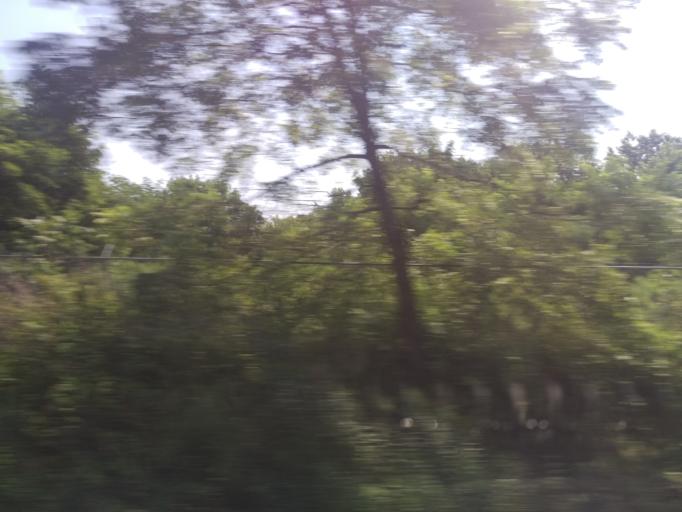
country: CA
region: Ontario
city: Ajax
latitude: 43.7957
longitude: -79.1172
